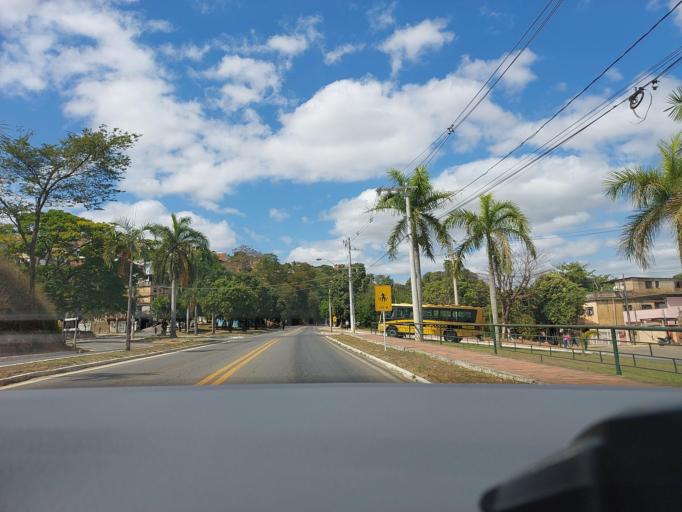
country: BR
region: Minas Gerais
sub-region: Muriae
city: Muriae
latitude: -21.1255
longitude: -42.3531
